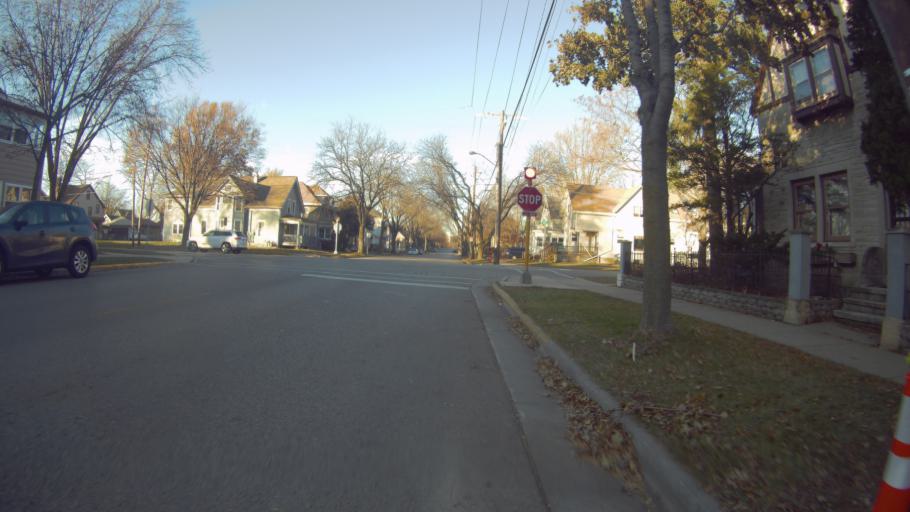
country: US
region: Wisconsin
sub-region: Dane County
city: Madison
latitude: 43.0618
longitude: -89.4041
